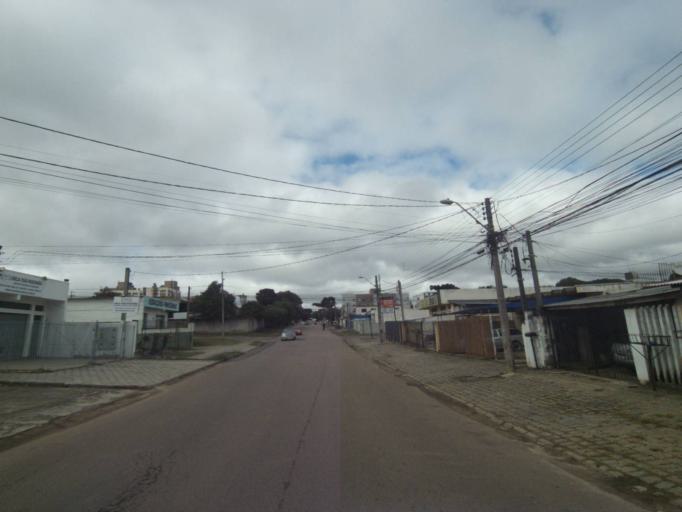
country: BR
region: Parana
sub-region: Sao Jose Dos Pinhais
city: Sao Jose dos Pinhais
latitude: -25.5164
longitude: -49.2990
